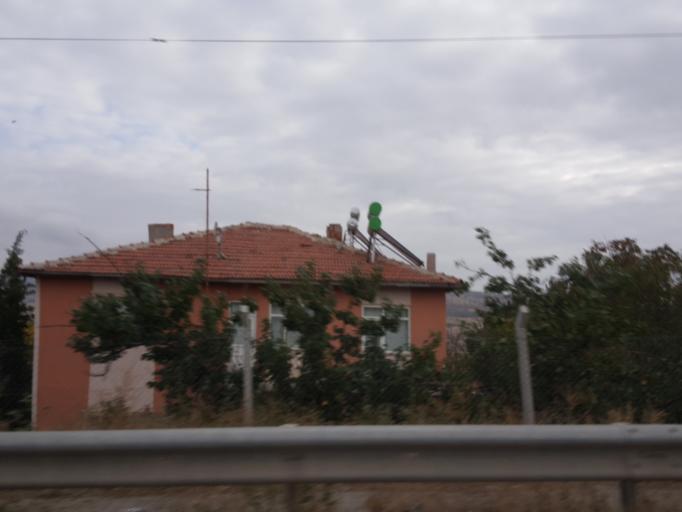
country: TR
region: Kirikkale
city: Keskin
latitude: 39.6696
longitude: 33.6110
